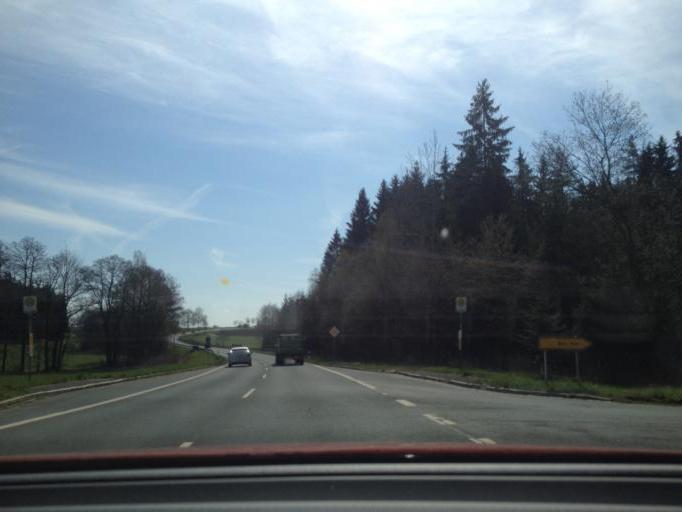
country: DE
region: Bavaria
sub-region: Upper Franconia
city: Grub
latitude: 50.0866
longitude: 11.9344
